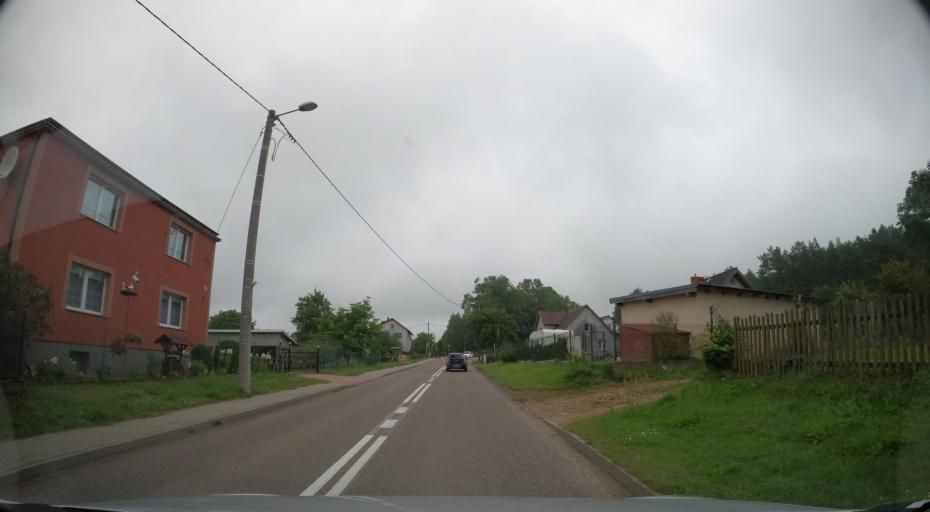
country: PL
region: Pomeranian Voivodeship
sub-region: Powiat wejherowski
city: Luzino
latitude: 54.4697
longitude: 18.0733
